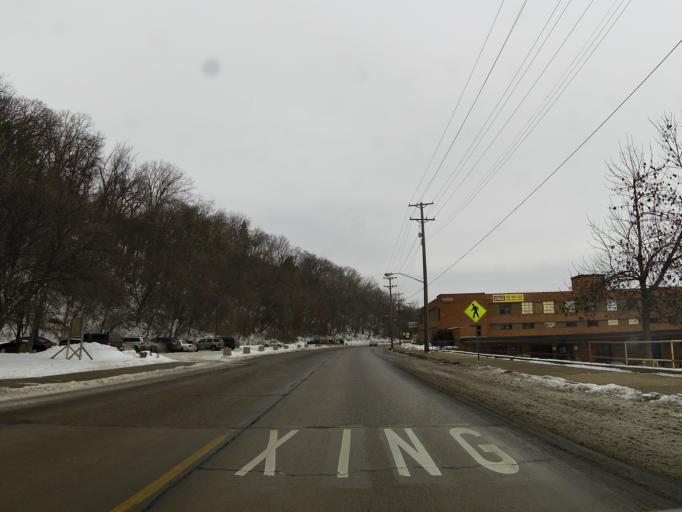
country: US
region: Minnesota
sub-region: Dakota County
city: South Saint Paul
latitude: 44.9089
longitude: -93.0502
